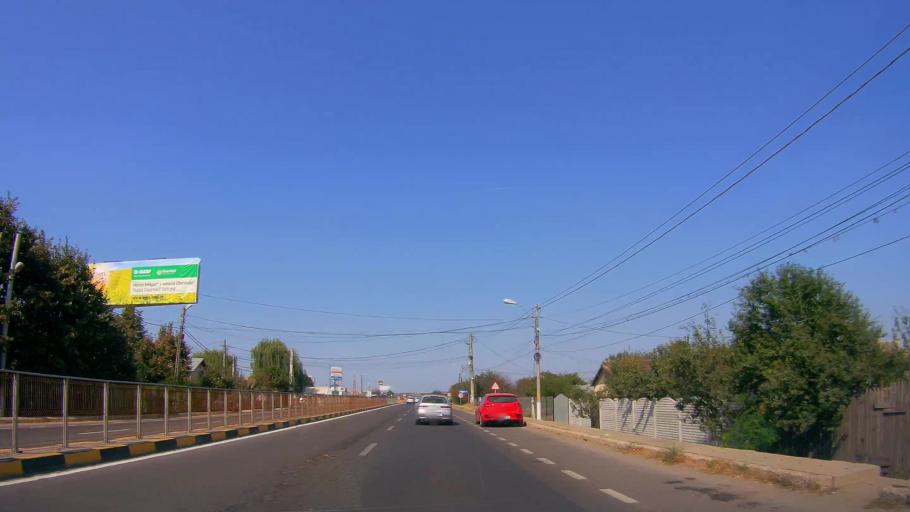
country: RO
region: Giurgiu
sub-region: Comuna Fratesti
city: Remus
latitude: 43.9478
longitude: 25.9802
